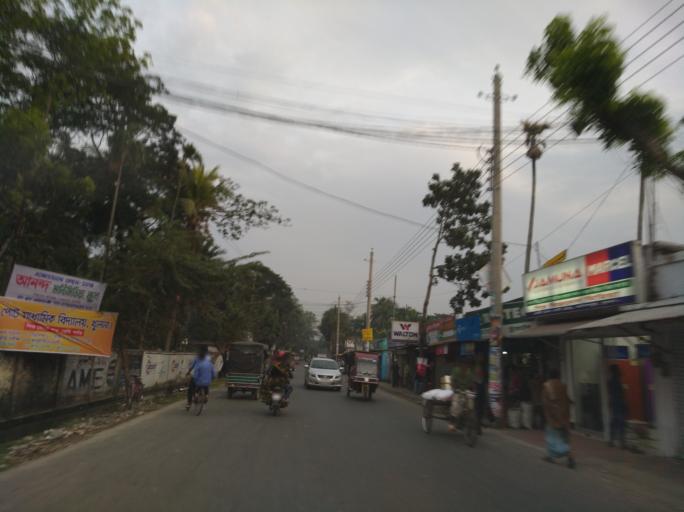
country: BD
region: Khulna
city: Khulna
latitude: 22.8417
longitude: 89.5440
